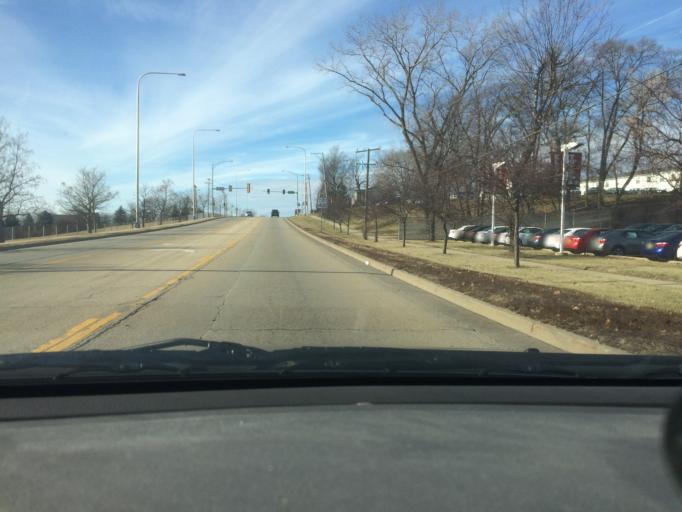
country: US
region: Illinois
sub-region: Kane County
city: Elgin
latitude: 42.0313
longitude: -88.2445
